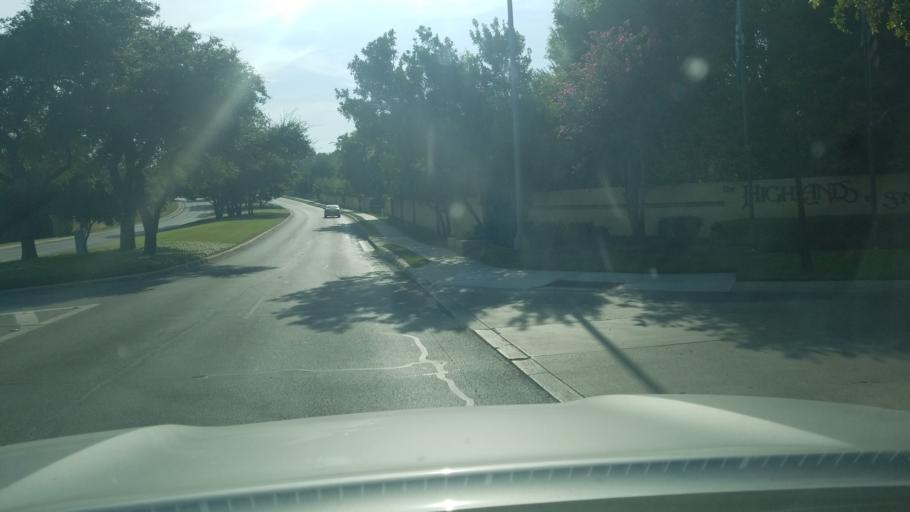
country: US
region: Texas
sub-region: Bexar County
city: Hollywood Park
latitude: 29.6267
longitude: -98.4986
